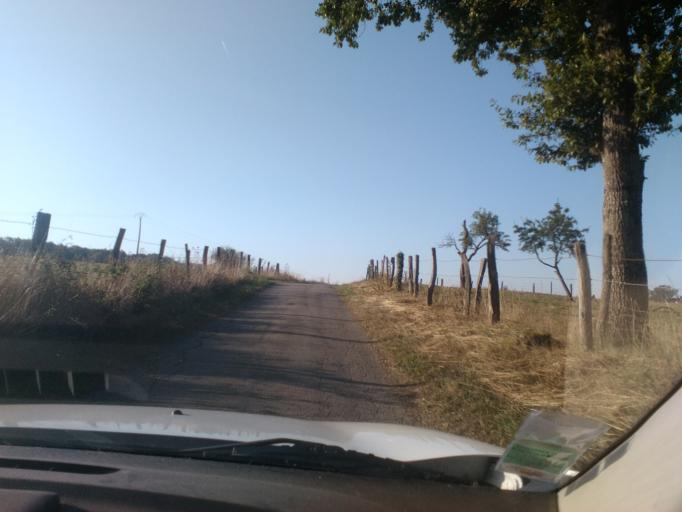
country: FR
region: Lorraine
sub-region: Departement des Vosges
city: Mirecourt
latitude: 48.2827
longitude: 6.1901
